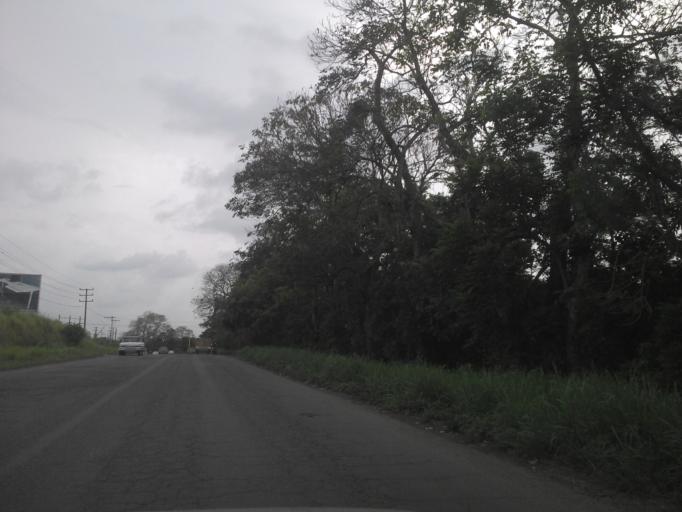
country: MX
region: Veracruz
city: Martinez de la Torre
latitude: 20.0802
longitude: -97.0415
